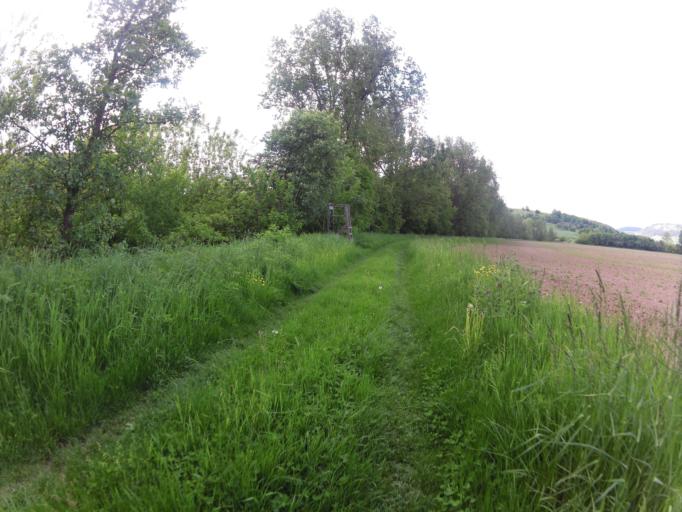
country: DE
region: Thuringia
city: Treffurt
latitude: 51.1198
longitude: 10.2489
